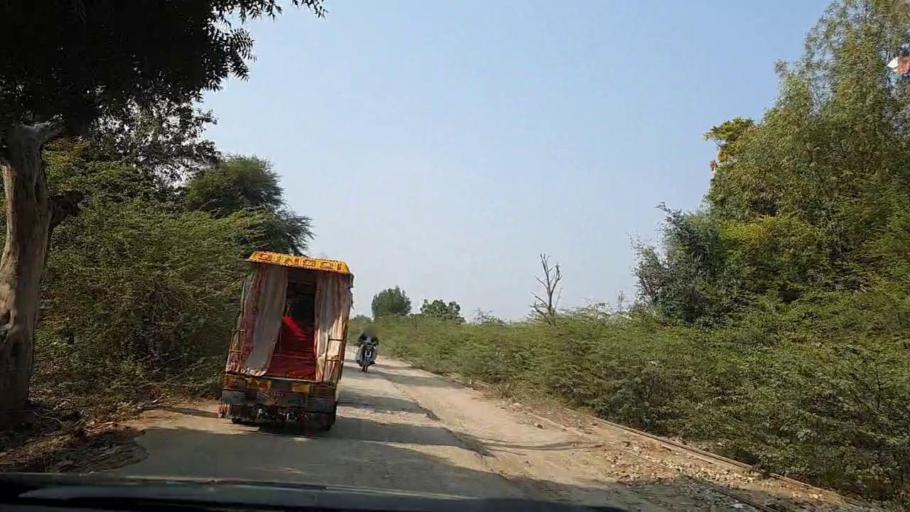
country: PK
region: Sindh
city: Sakrand
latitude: 26.1404
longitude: 68.2777
